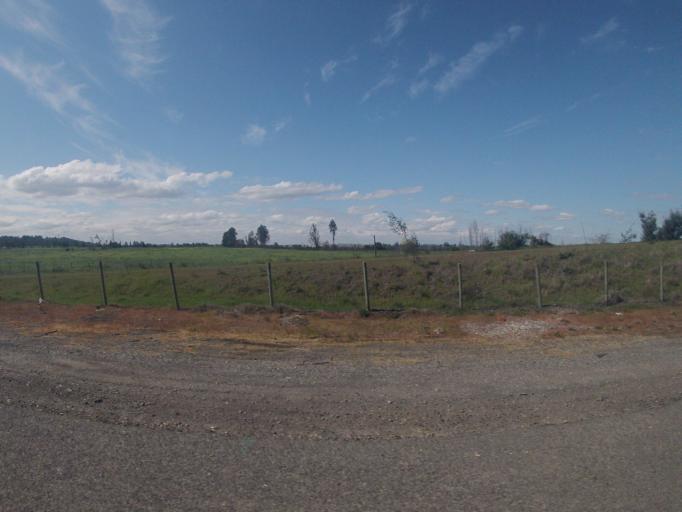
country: CL
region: Biobio
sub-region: Provincia de Biobio
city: Los Angeles
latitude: -37.4511
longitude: -72.4078
